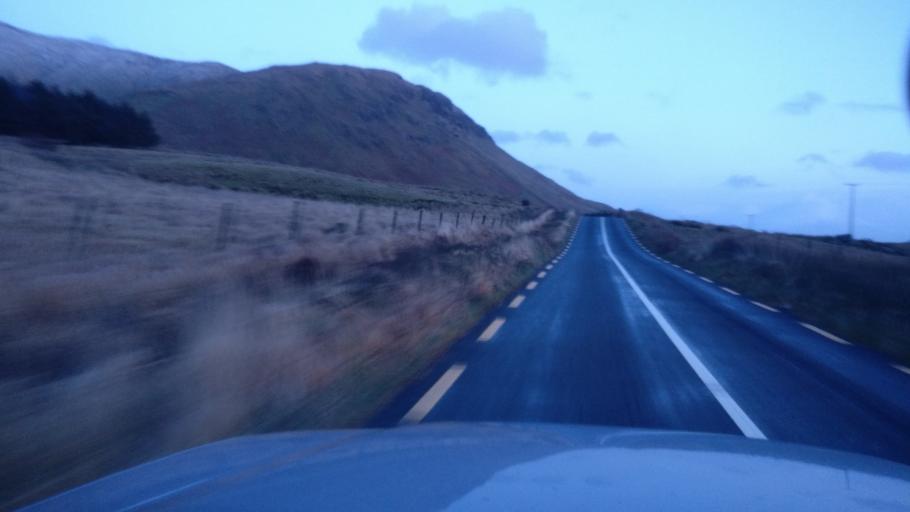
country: IE
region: Connaught
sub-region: Maigh Eo
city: Westport
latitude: 53.5501
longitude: -9.6329
